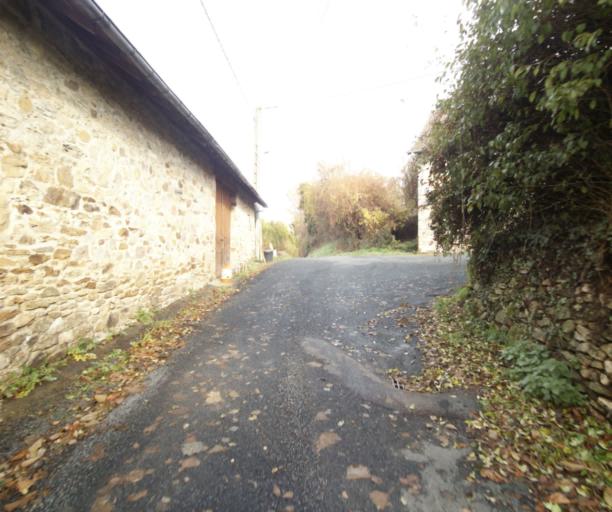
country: FR
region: Limousin
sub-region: Departement de la Correze
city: Chameyrat
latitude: 45.2231
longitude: 1.7257
